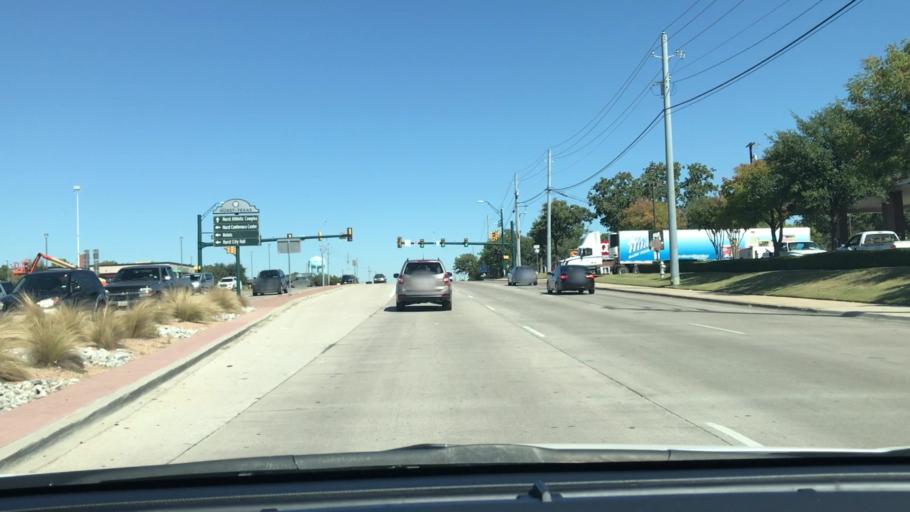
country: US
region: Texas
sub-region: Tarrant County
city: Hurst
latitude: 32.8402
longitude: -97.1862
